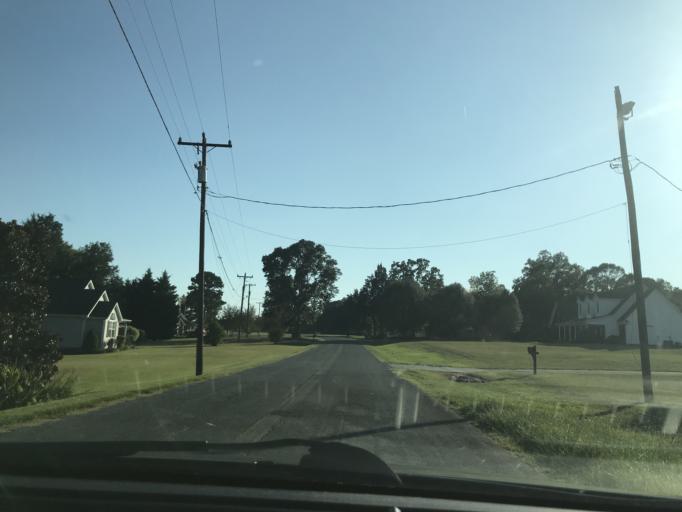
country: US
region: North Carolina
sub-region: Cleveland County
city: Boiling Springs
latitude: 35.1570
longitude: -81.7394
